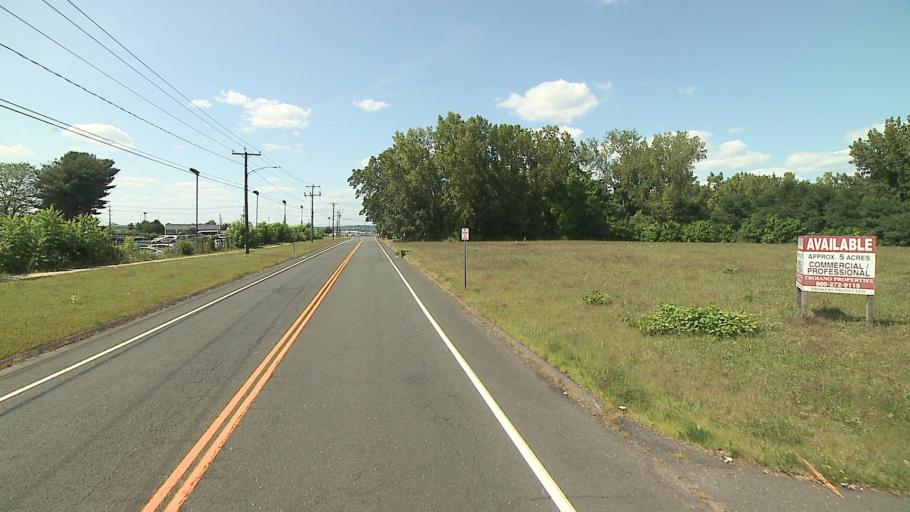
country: US
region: Connecticut
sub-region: Hartford County
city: Windsor Locks
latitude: 41.9287
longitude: -72.6671
